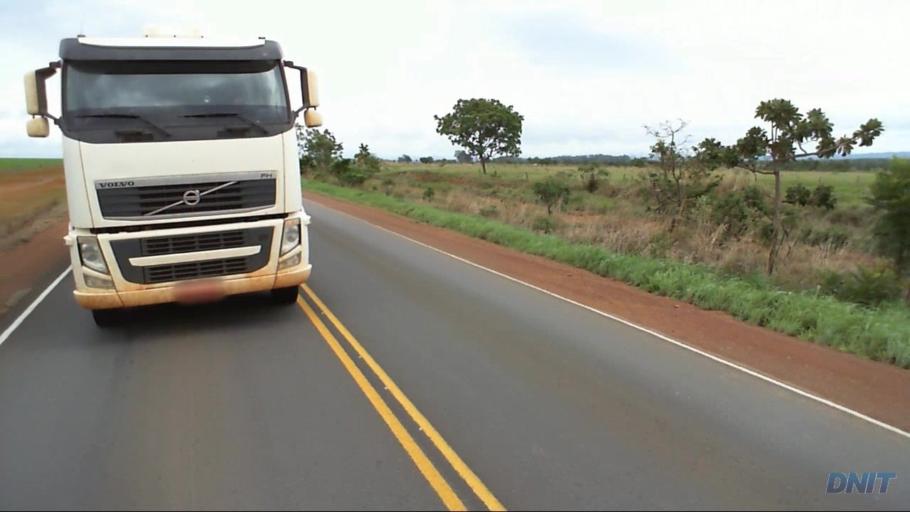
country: BR
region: Goias
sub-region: Padre Bernardo
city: Padre Bernardo
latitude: -15.3451
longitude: -48.2332
